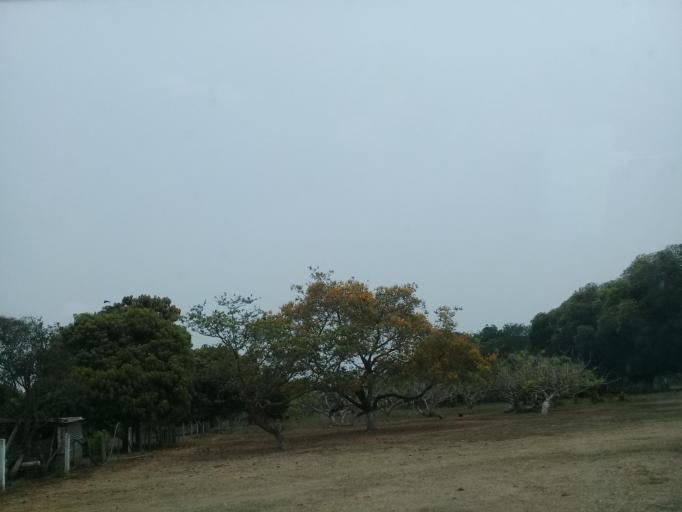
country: MX
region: Veracruz
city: Jamapa
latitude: 19.0418
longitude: -96.1955
